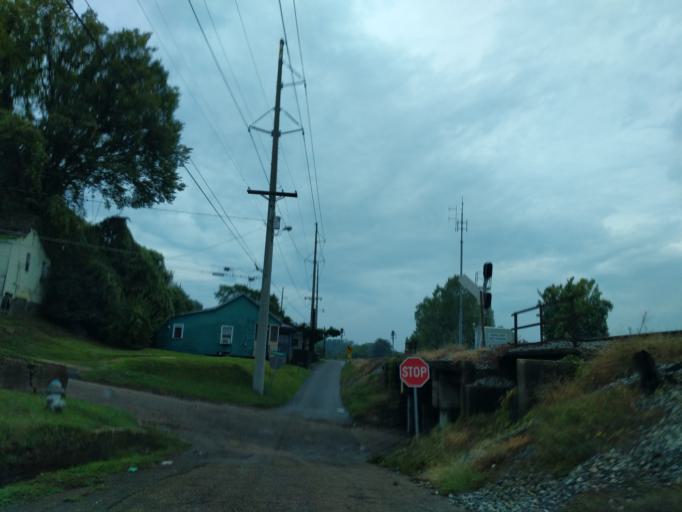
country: US
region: Mississippi
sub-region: Warren County
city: Vicksburg
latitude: 32.3378
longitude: -90.8894
